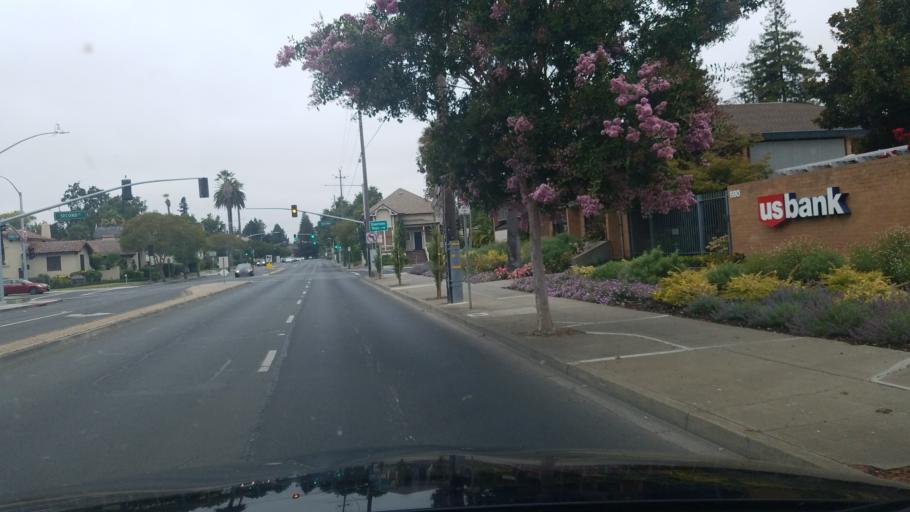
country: US
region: California
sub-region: Napa County
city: Napa
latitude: 38.2959
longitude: -122.2936
